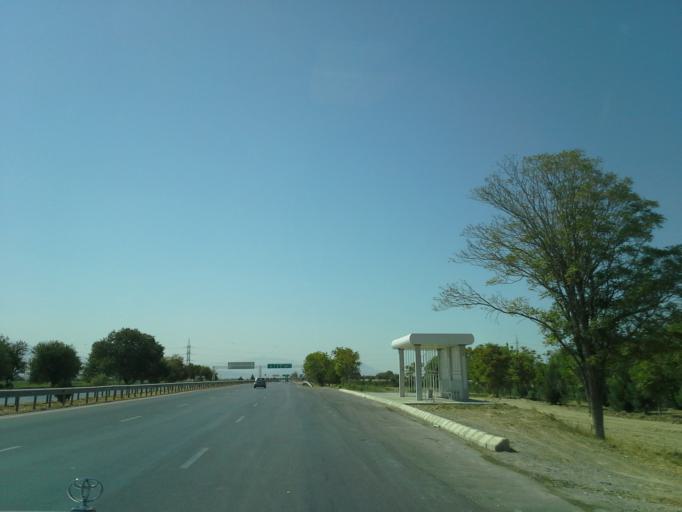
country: TM
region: Ahal
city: Annau
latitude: 37.9035
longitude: 58.5533
